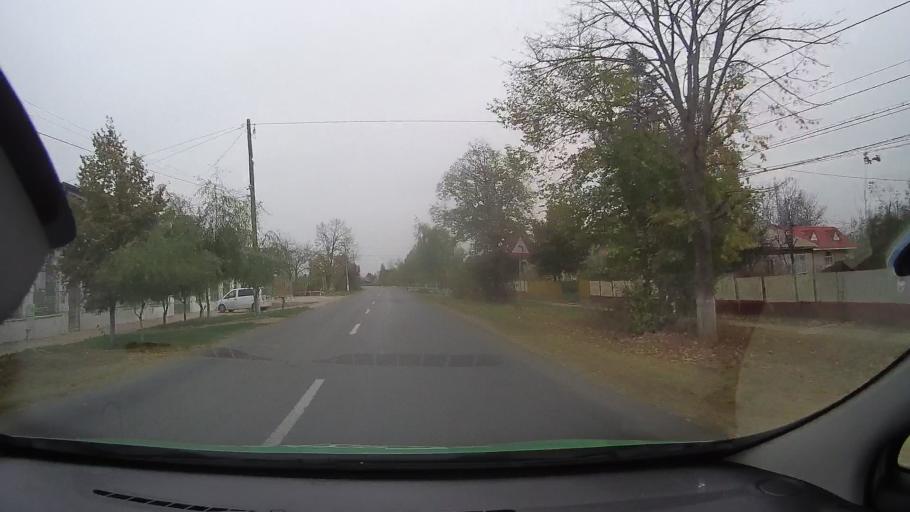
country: RO
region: Ialomita
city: Tandarei
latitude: 44.6520
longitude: 27.6549
